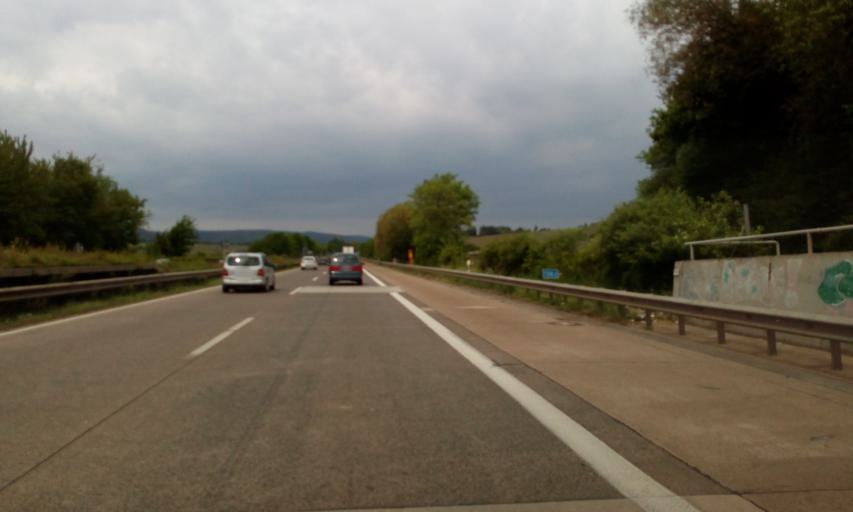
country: DE
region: Rheinland-Pfalz
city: Schweich
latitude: 49.8202
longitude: 6.7588
